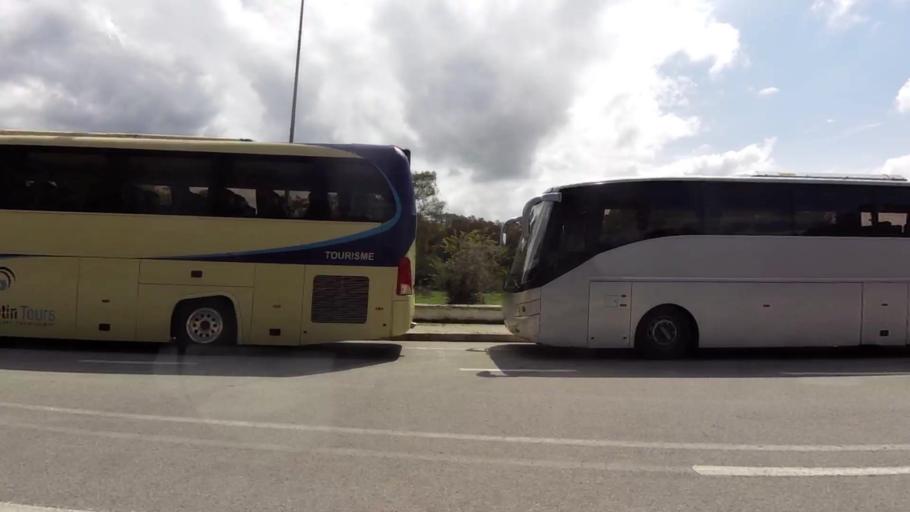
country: MA
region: Tanger-Tetouan
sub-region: Tanger-Assilah
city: Tangier
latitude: 35.7804
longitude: -5.7640
